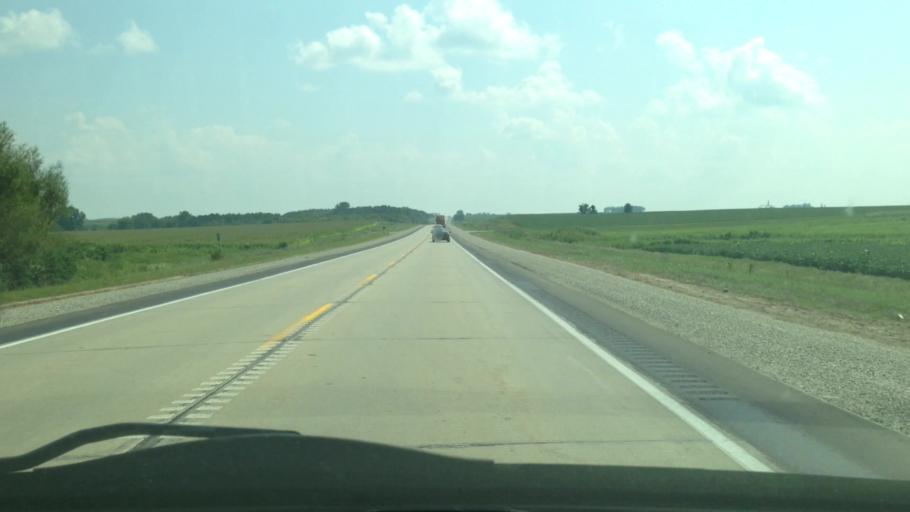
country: US
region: Iowa
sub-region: Howard County
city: Cresco
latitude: 43.3974
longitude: -92.2984
